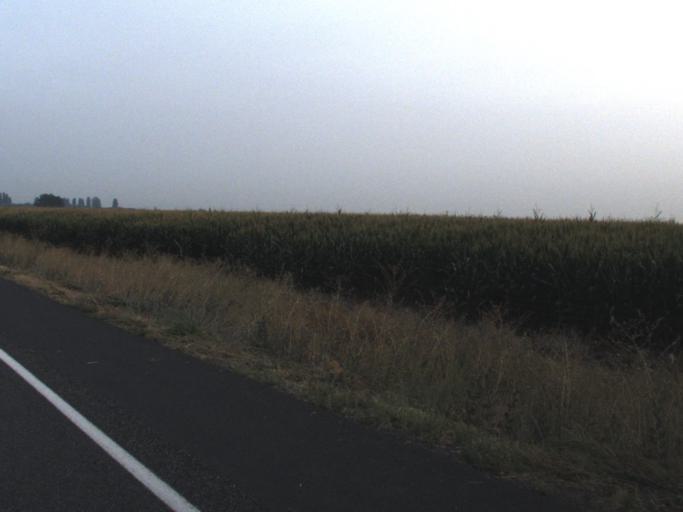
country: US
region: Washington
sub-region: Yakima County
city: Toppenish
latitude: 46.3211
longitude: -120.3210
